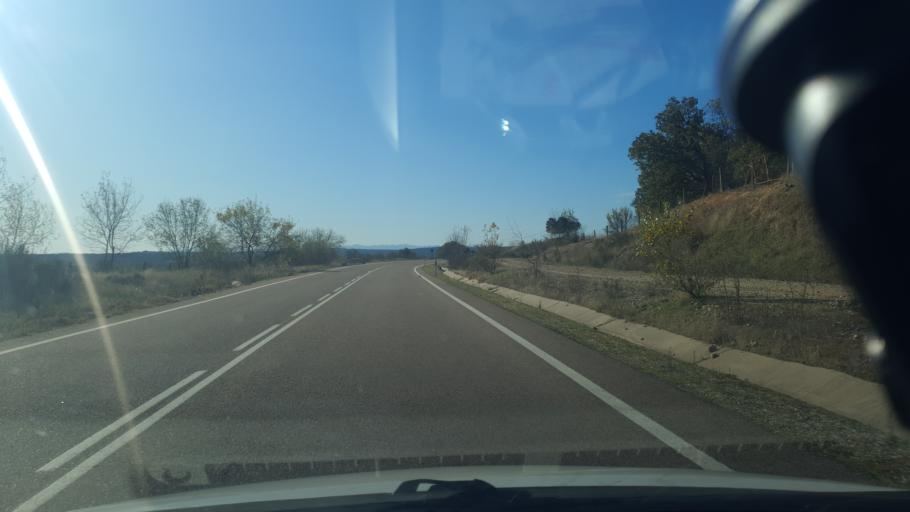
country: ES
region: Castille and Leon
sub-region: Provincia de Avila
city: Poyales del Hoyo
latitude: 40.1503
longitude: -5.1897
